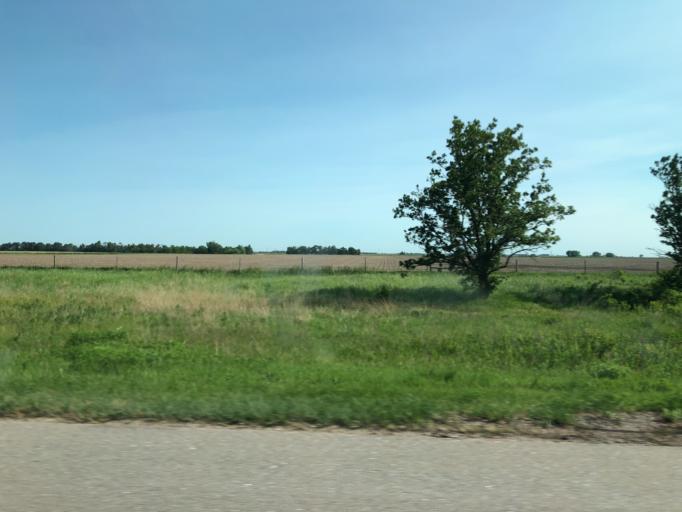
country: US
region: Nebraska
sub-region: Seward County
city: Seward
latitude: 40.8222
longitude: -97.1619
